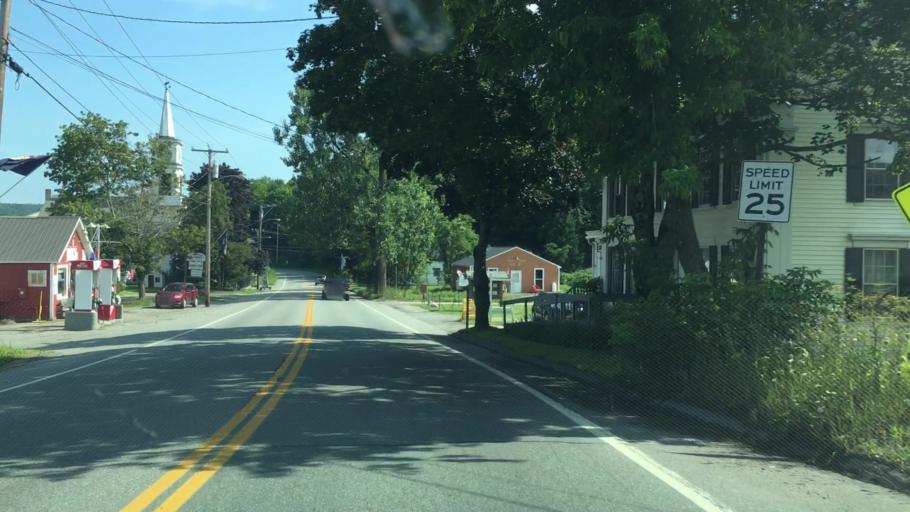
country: US
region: Maine
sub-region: Waldo County
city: Frankfort
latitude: 44.6085
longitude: -68.8745
